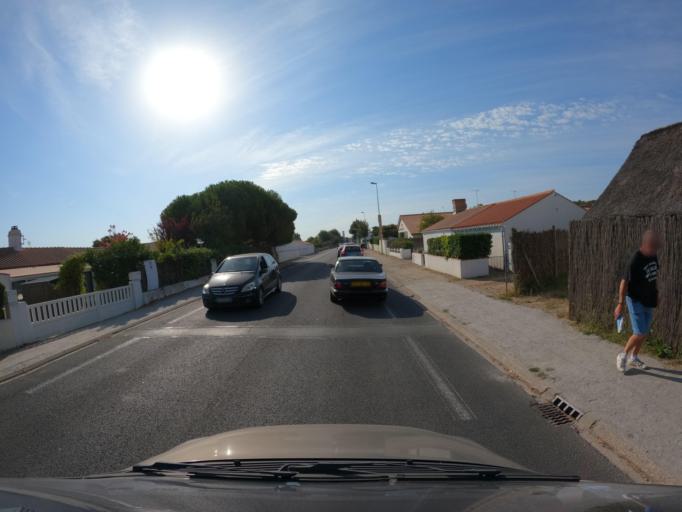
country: FR
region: Pays de la Loire
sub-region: Departement de la Vendee
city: Saint-Jean-de-Monts
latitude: 46.7983
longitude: -2.0725
